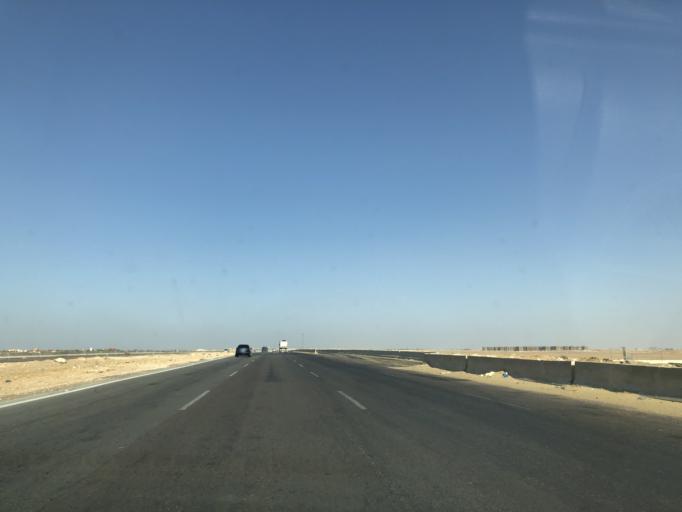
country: EG
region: Muhafazat al Minufiyah
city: Ashmun
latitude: 30.0676
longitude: 30.8666
